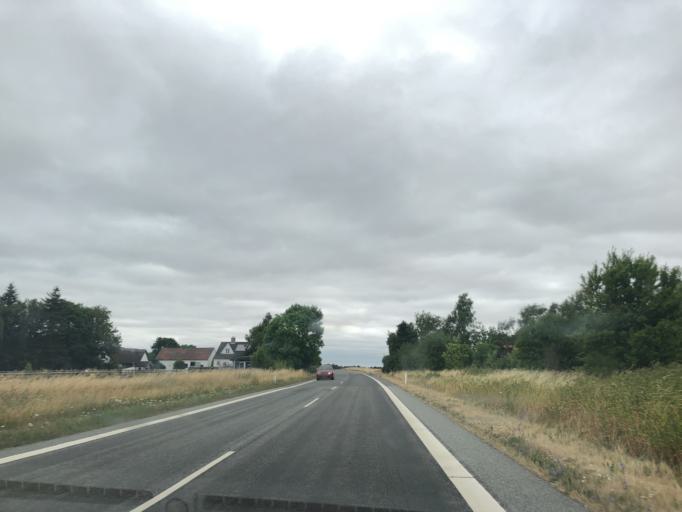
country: DK
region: Zealand
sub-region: Slagelse Kommune
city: Skaelskor
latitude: 55.2286
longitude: 11.3101
